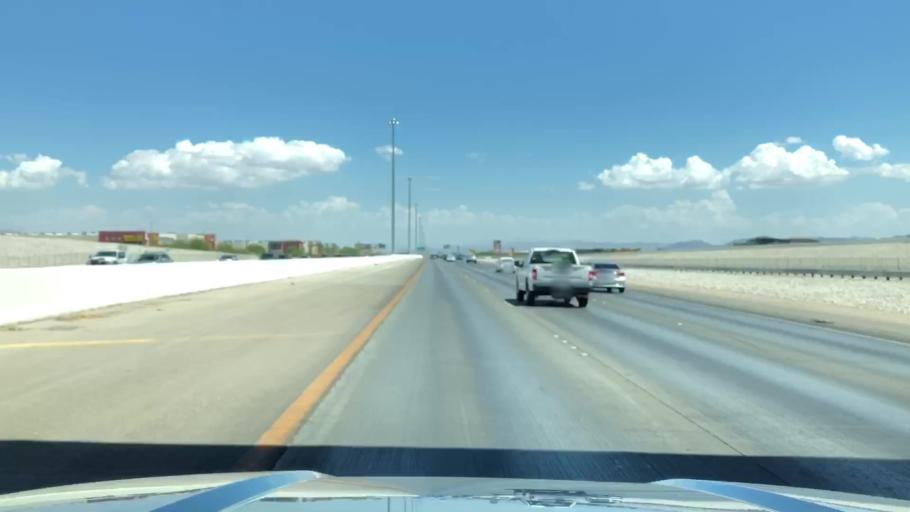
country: US
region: Nevada
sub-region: Clark County
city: Spring Valley
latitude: 36.0661
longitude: -115.2603
